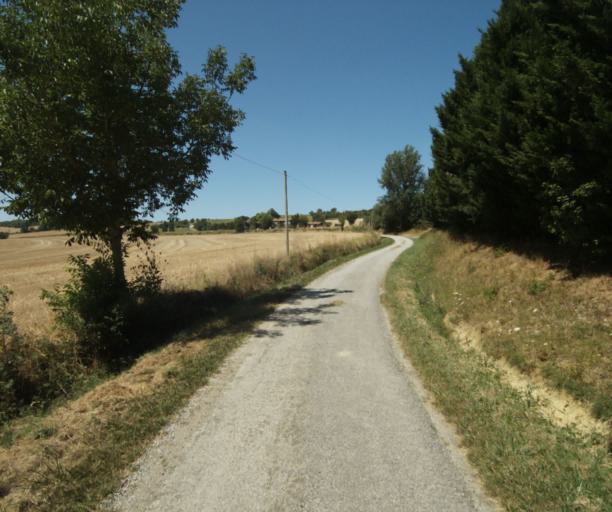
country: FR
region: Midi-Pyrenees
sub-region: Departement de la Haute-Garonne
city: Saint-Felix-Lauragais
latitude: 43.4925
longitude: 1.8834
